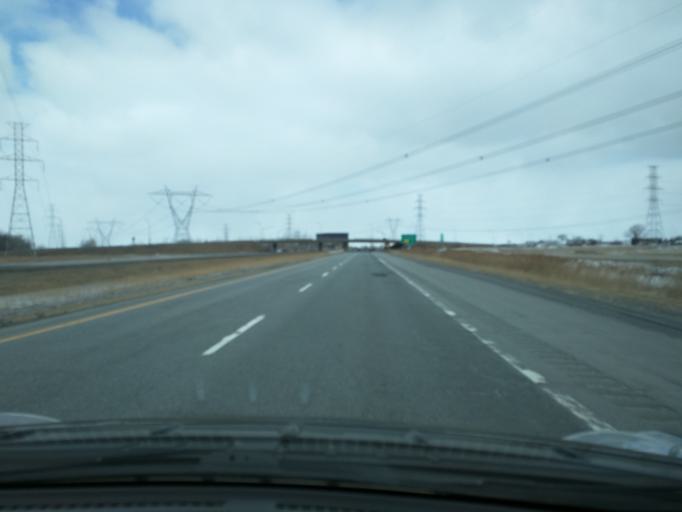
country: CA
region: Quebec
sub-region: Monteregie
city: Sainte-Julie
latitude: 45.6003
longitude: -73.3734
